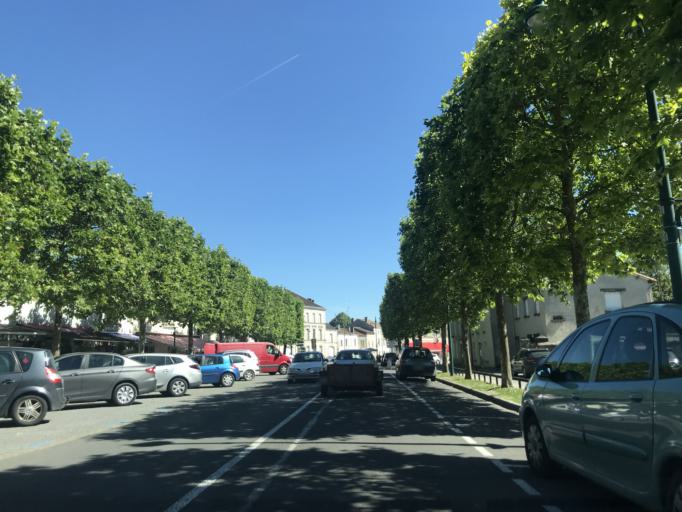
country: FR
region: Poitou-Charentes
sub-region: Departement de la Charente
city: Barbezieux-Saint-Hilaire
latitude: 45.4731
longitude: -0.1515
